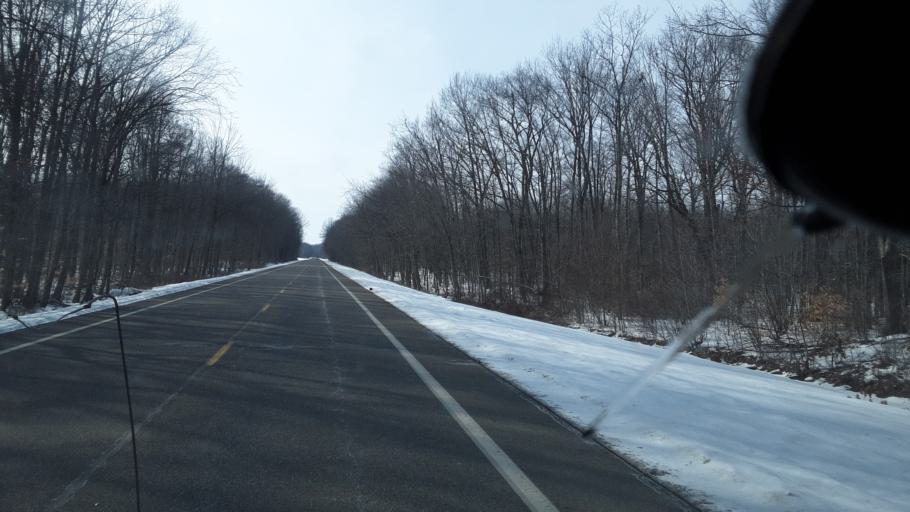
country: US
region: Ohio
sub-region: Portage County
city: Ravenna
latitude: 41.0331
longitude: -81.1847
